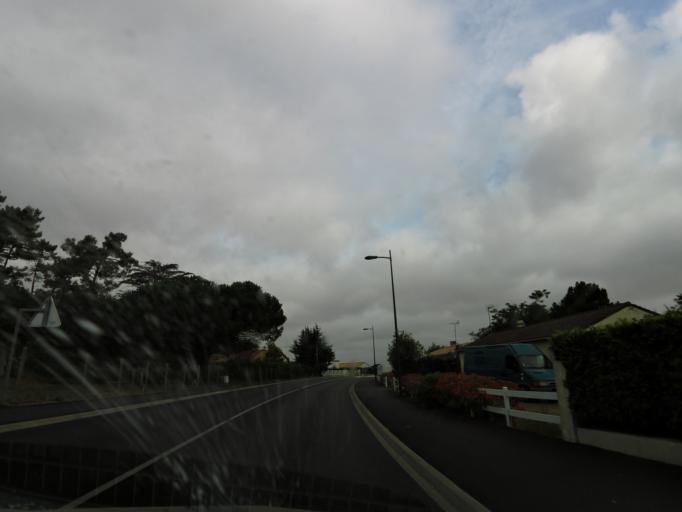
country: FR
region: Pays de la Loire
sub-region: Departement de la Vendee
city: Longeville-sur-Mer
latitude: 46.4094
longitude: -1.4938
